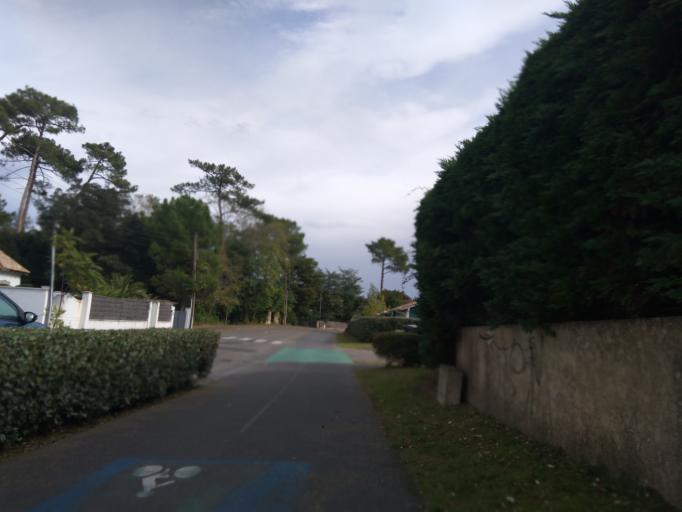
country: FR
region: Aquitaine
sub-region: Departement des Landes
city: Capbreton
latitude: 43.6397
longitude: -1.4384
